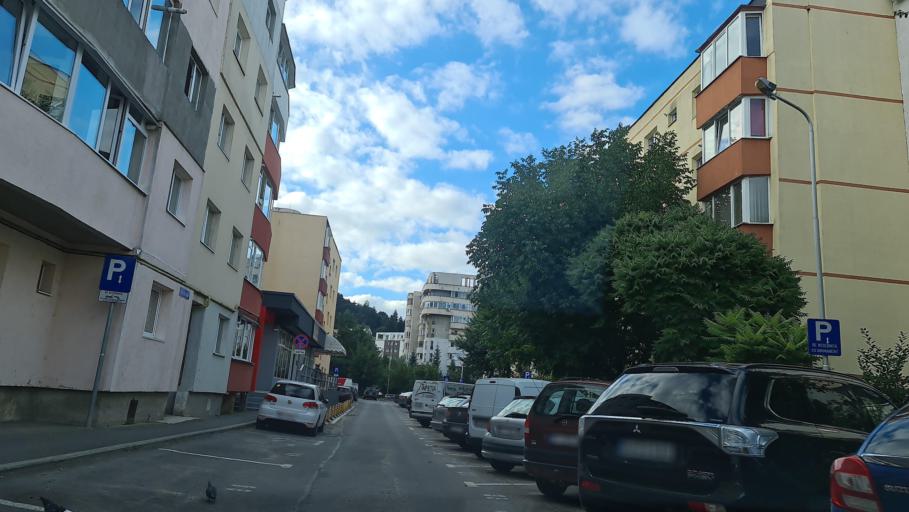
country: RO
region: Brasov
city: Brasov
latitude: 45.6421
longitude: 25.6208
